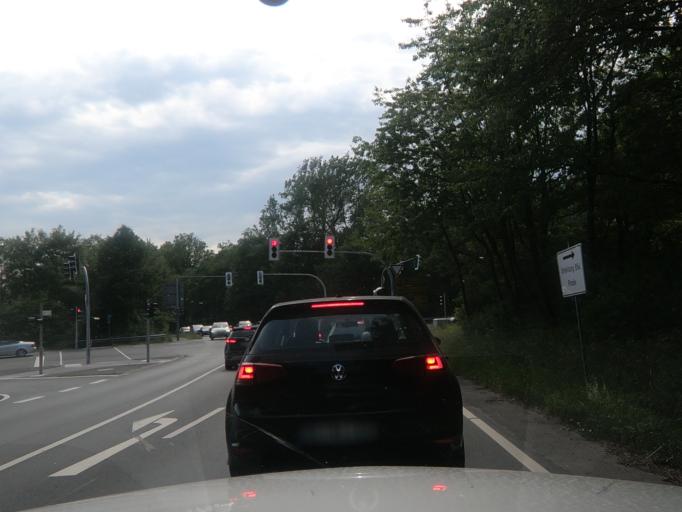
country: DE
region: North Rhine-Westphalia
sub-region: Regierungsbezirk Arnsberg
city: Olpe
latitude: 51.0408
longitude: 7.8640
